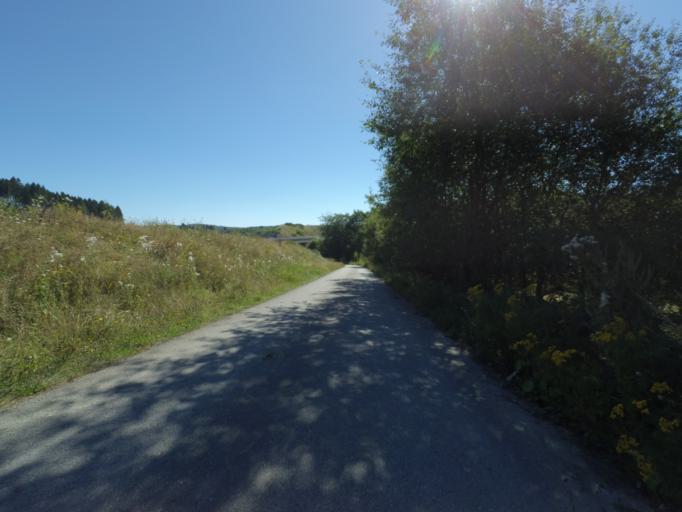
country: DE
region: Rheinland-Pfalz
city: Horscheid
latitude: 50.2097
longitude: 6.8739
